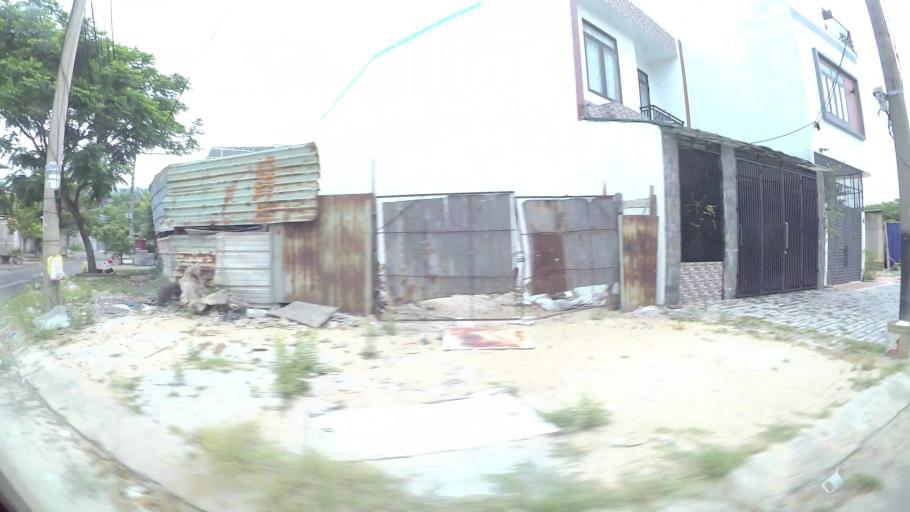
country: VN
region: Da Nang
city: Da Nang
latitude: 16.0967
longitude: 108.2330
